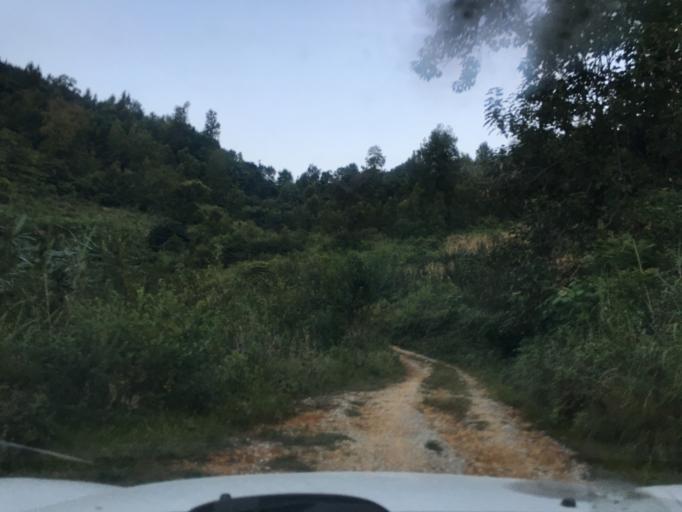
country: CN
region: Guangxi Zhuangzu Zizhiqu
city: Xinzhou
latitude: 25.3512
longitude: 105.7413
